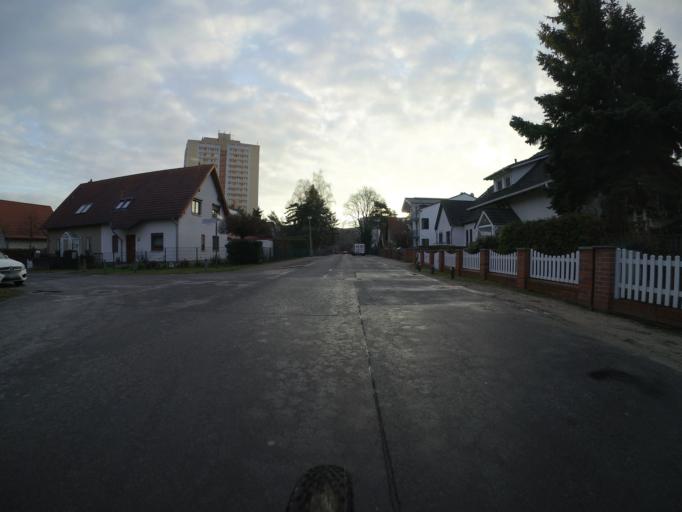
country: DE
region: Berlin
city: Marzahn
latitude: 52.5421
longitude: 13.5535
